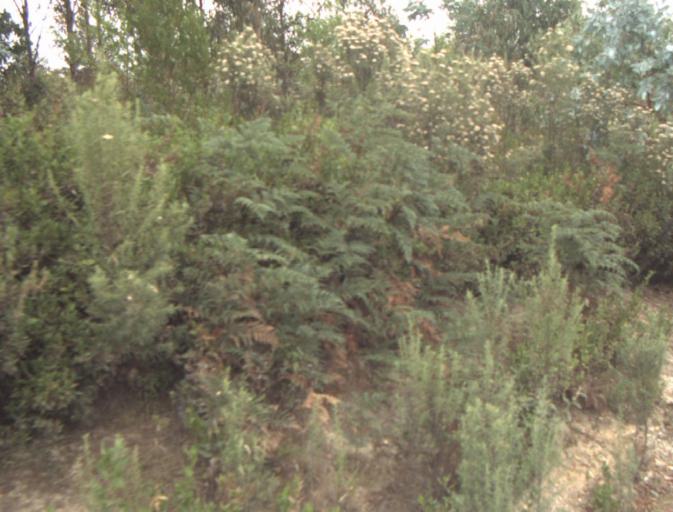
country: AU
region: Tasmania
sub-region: Launceston
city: Mayfield
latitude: -41.1599
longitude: 147.1732
